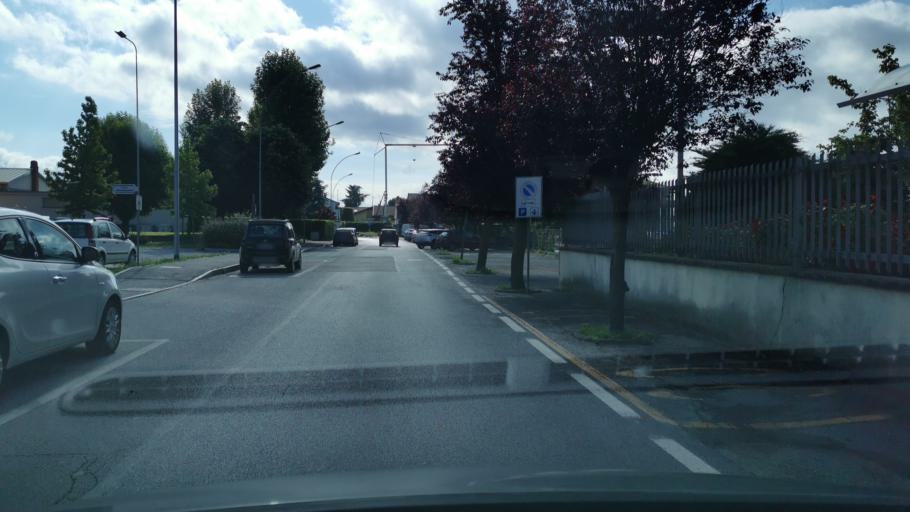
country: IT
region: Piedmont
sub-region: Provincia di Torino
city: Cambiano
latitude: 44.9702
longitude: 7.7785
